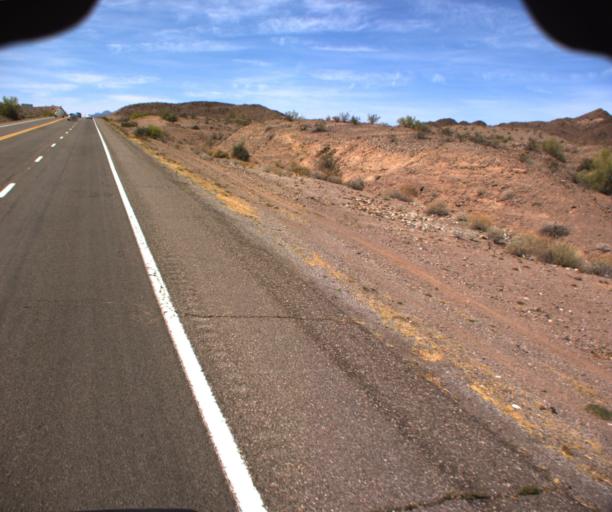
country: US
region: Arizona
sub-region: La Paz County
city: Cienega Springs
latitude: 34.3726
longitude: -114.1622
